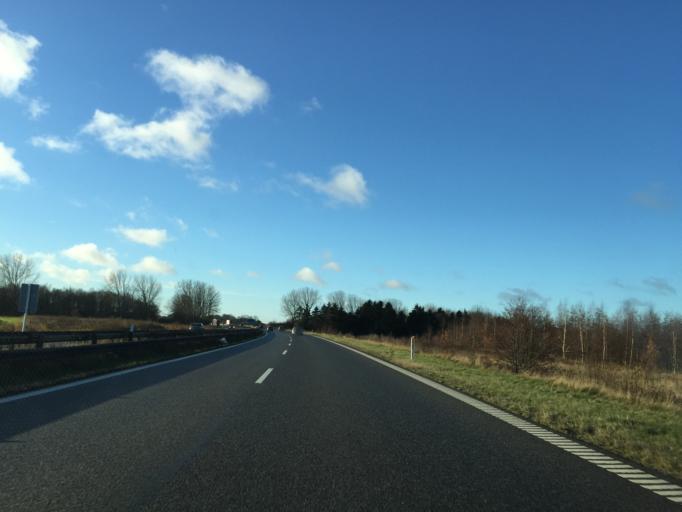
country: DK
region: Zealand
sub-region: Slagelse Kommune
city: Korsor
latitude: 55.3604
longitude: 11.1663
